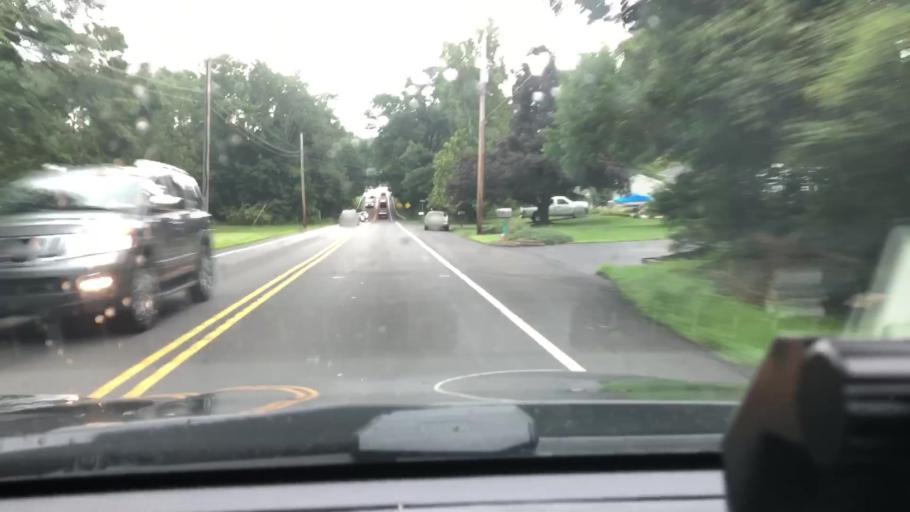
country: US
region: Pennsylvania
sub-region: Montgomery County
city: Pennsburg
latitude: 40.3760
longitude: -75.5152
